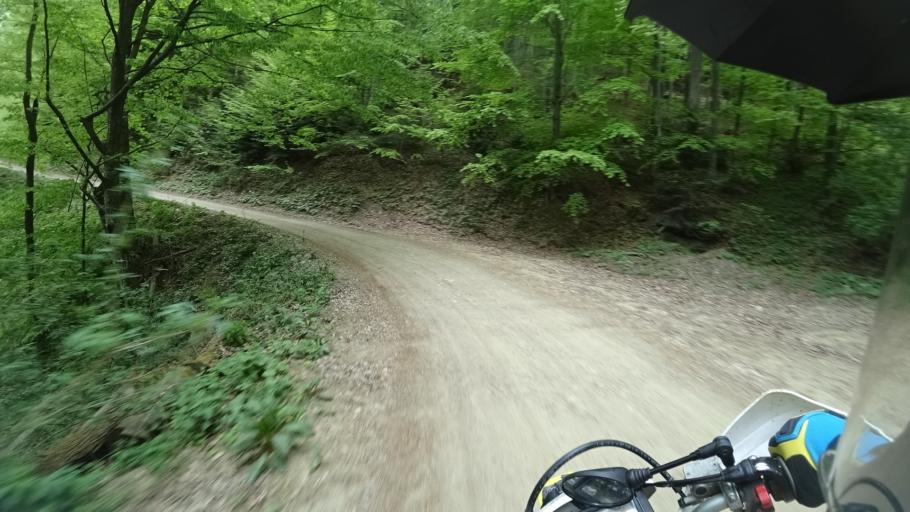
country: HR
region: Grad Zagreb
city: Kasina
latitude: 45.9057
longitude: 15.9860
